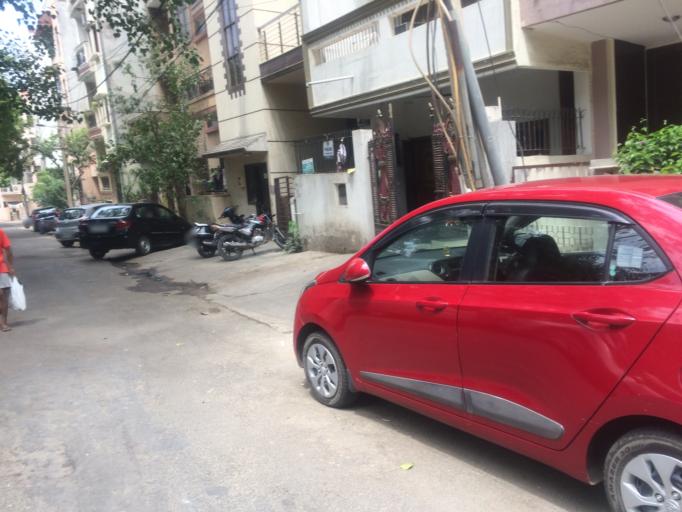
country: IN
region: Uttar Pradesh
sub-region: Gautam Buddha Nagar
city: Noida
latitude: 28.5601
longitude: 77.2581
